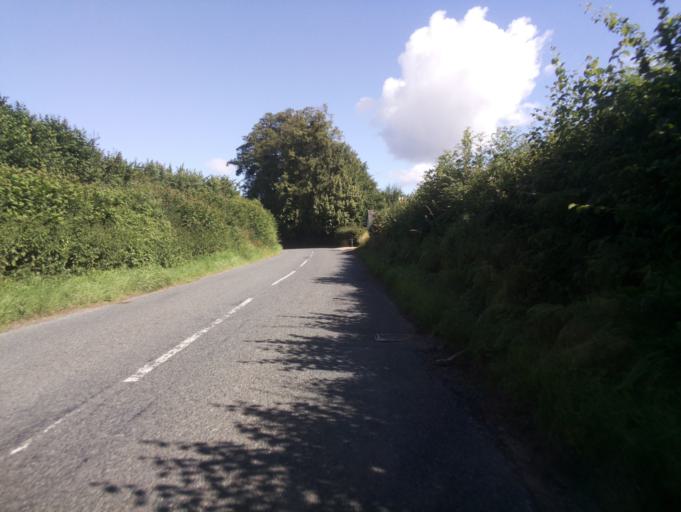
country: GB
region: England
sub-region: Herefordshire
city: Yatton
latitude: 51.9470
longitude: -2.5320
